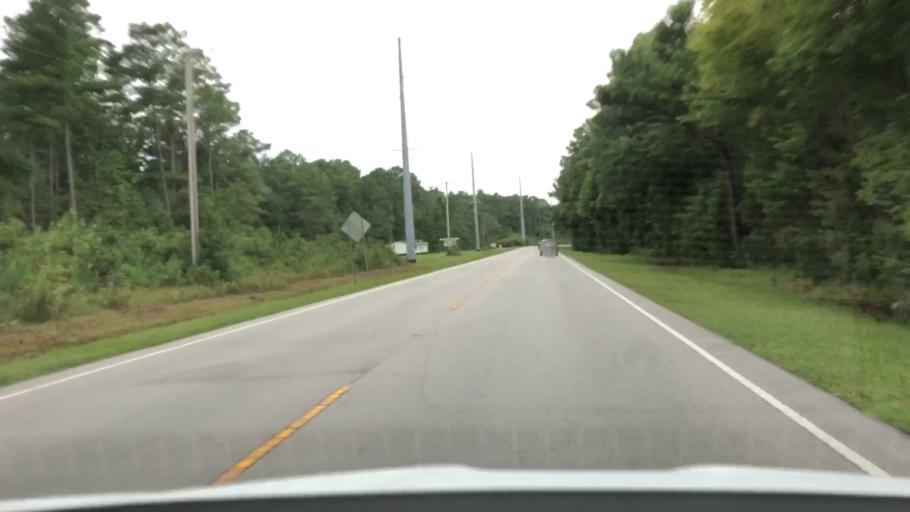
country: US
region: North Carolina
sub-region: Carteret County
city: Cape Carteret
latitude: 34.7462
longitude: -77.0901
